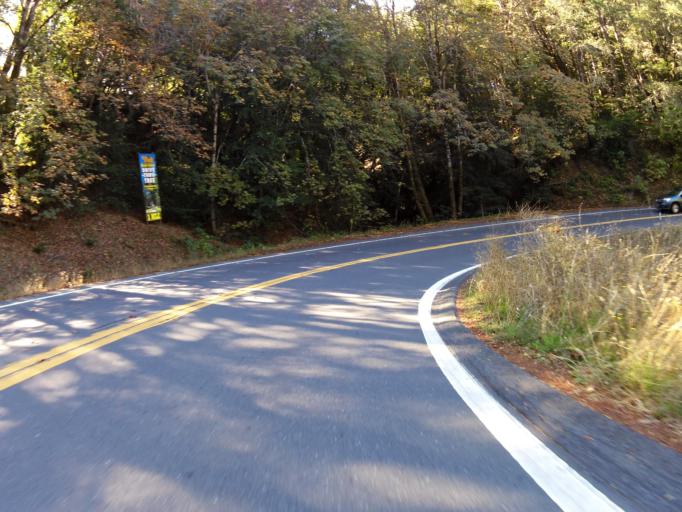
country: US
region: California
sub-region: Humboldt County
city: Redway
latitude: 39.8663
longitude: -123.7173
